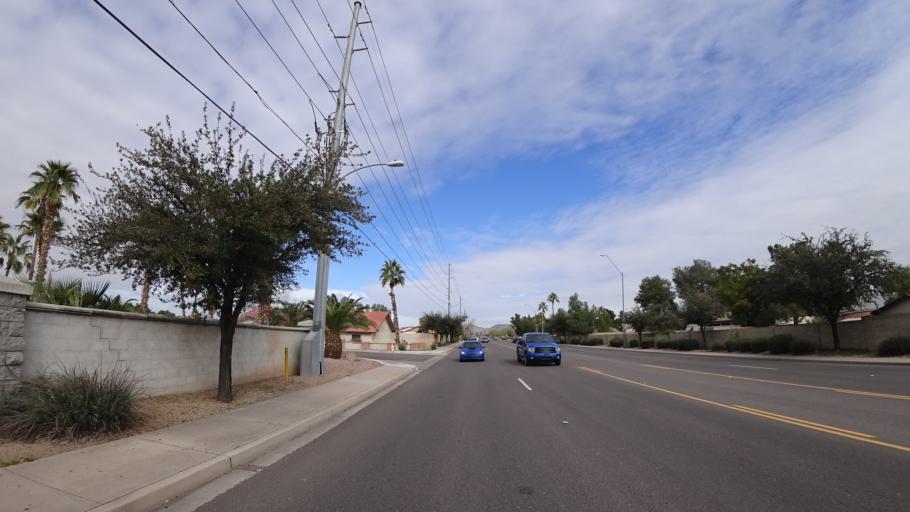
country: US
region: Arizona
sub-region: Maricopa County
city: Peoria
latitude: 33.6488
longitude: -112.1865
